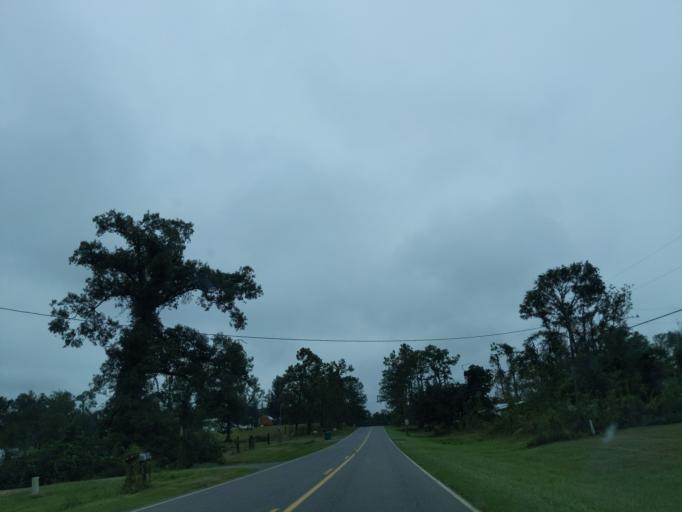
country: US
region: Florida
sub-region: Jackson County
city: Sneads
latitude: 30.7306
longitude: -84.9370
